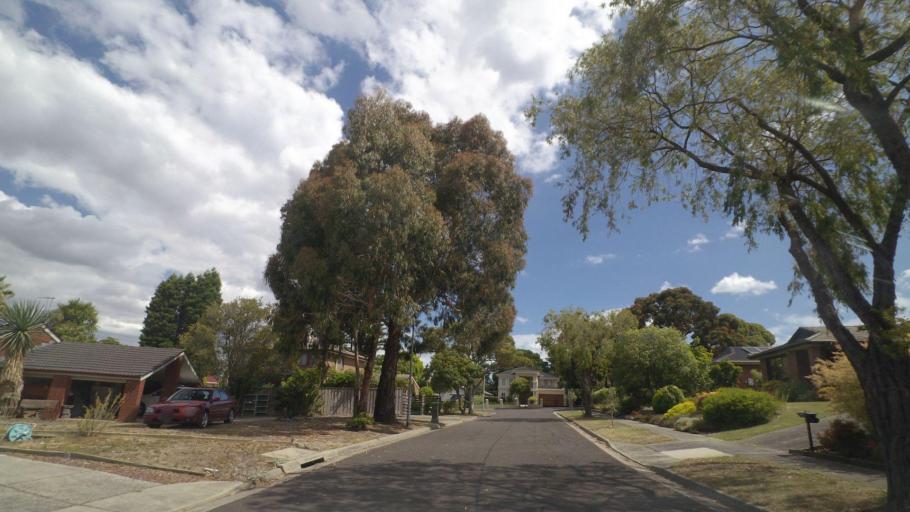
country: AU
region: Victoria
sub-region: Knox
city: Wantirna
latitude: -37.8629
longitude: 145.2214
